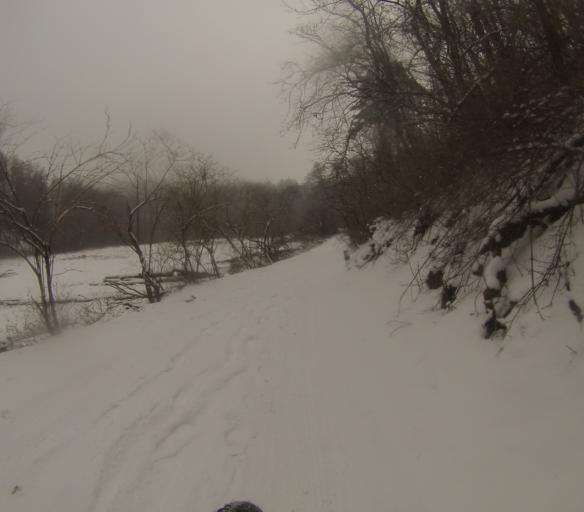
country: CZ
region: South Moravian
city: Zelesice
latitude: 49.1293
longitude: 16.5548
